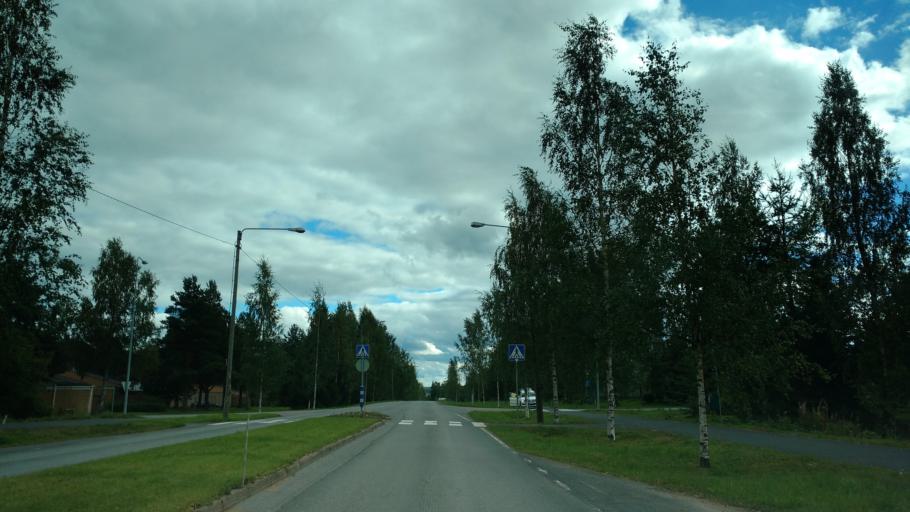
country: FI
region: Haeme
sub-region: Forssa
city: Ypaejae
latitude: 60.8069
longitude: 23.2753
